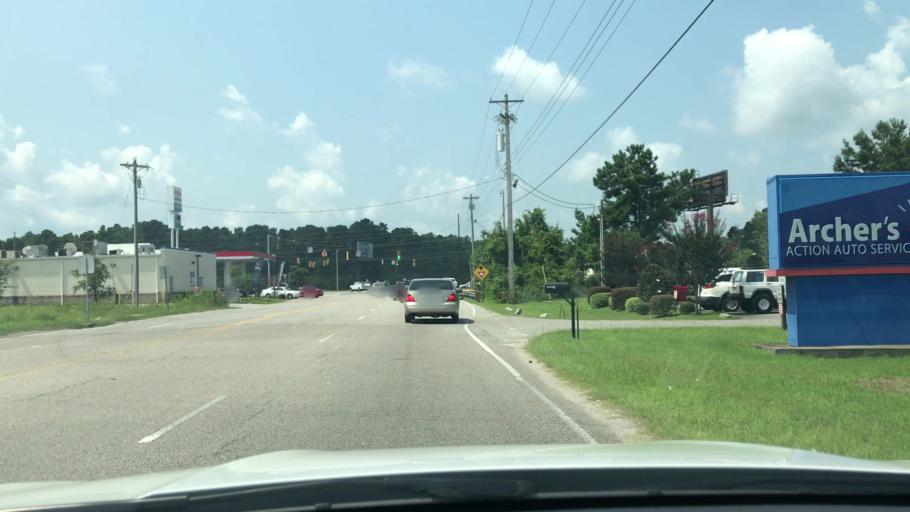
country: US
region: South Carolina
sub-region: Horry County
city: Red Hill
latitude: 33.7765
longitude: -78.9818
